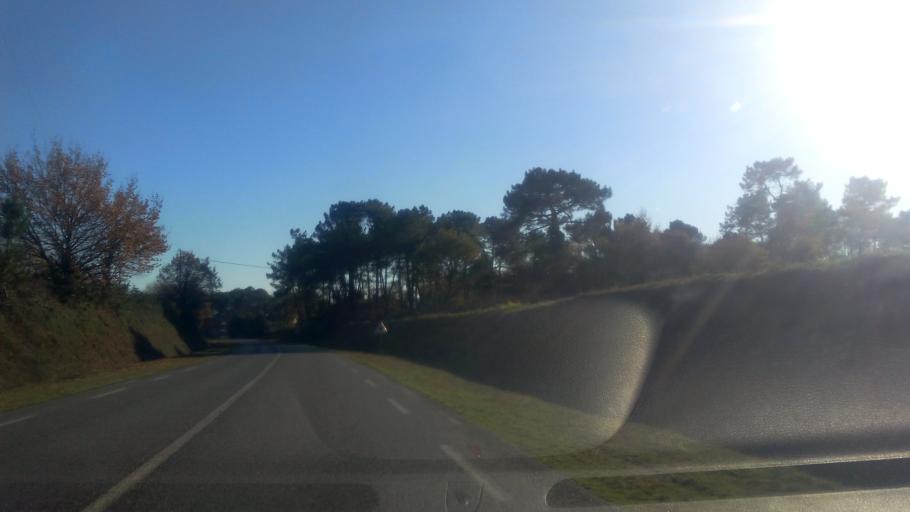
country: FR
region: Brittany
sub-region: Departement du Morbihan
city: Saint-Perreux
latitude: 47.6702
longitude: -2.1129
